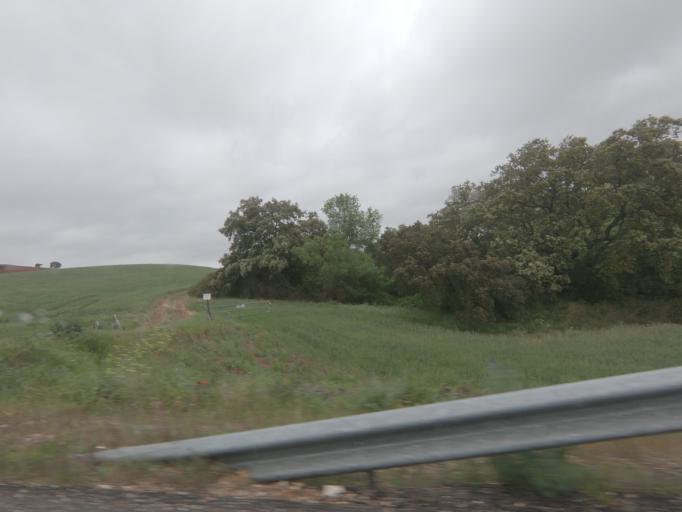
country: ES
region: Extremadura
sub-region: Provincia de Badajoz
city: La Roca de la Sierra
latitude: 39.0574
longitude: -6.7762
